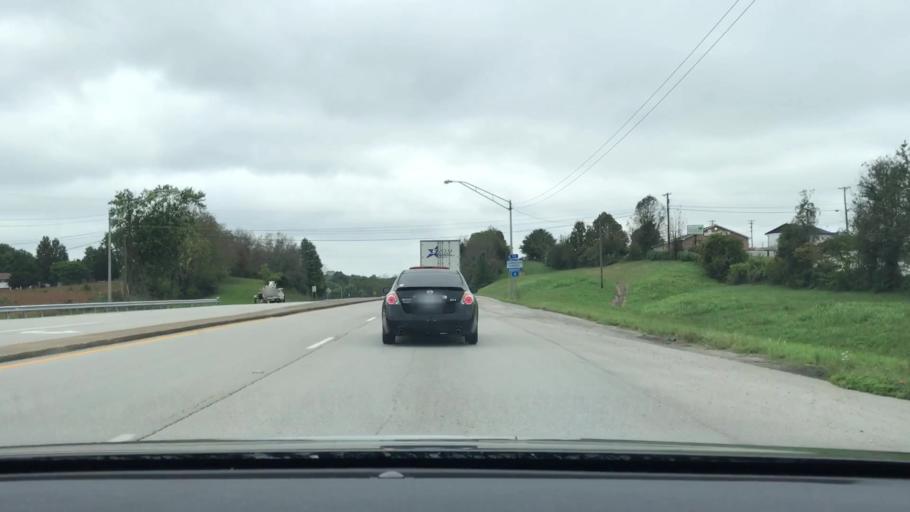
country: US
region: Kentucky
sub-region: Pulaski County
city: Somerset
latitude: 37.0935
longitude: -84.6305
